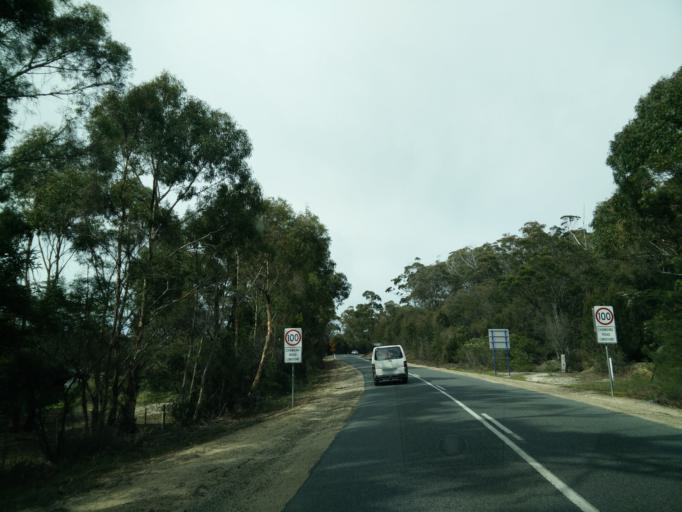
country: AU
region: Tasmania
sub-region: Break O'Day
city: St Helens
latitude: -41.8852
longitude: 148.2992
